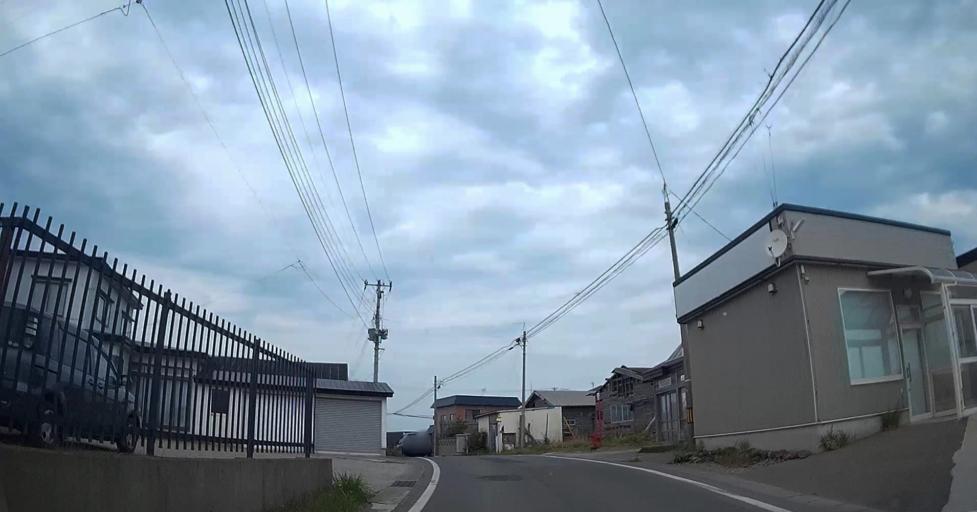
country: JP
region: Aomori
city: Shimokizukuri
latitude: 41.0259
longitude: 140.3268
